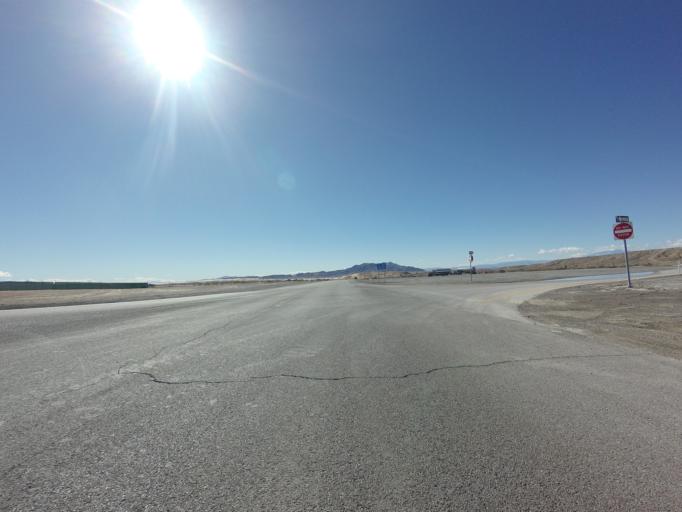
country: US
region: Nevada
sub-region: Clark County
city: Nellis Air Force Base
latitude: 36.3096
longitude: -114.9527
